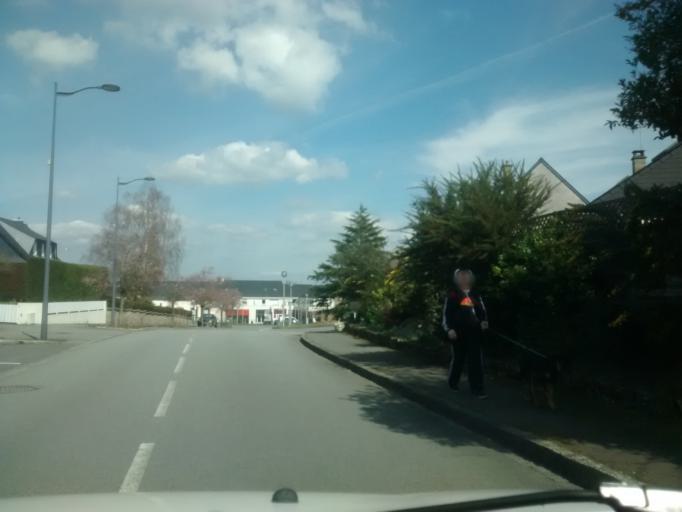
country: FR
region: Brittany
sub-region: Departement d'Ille-et-Vilaine
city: Brece
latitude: 48.1095
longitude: -1.4841
